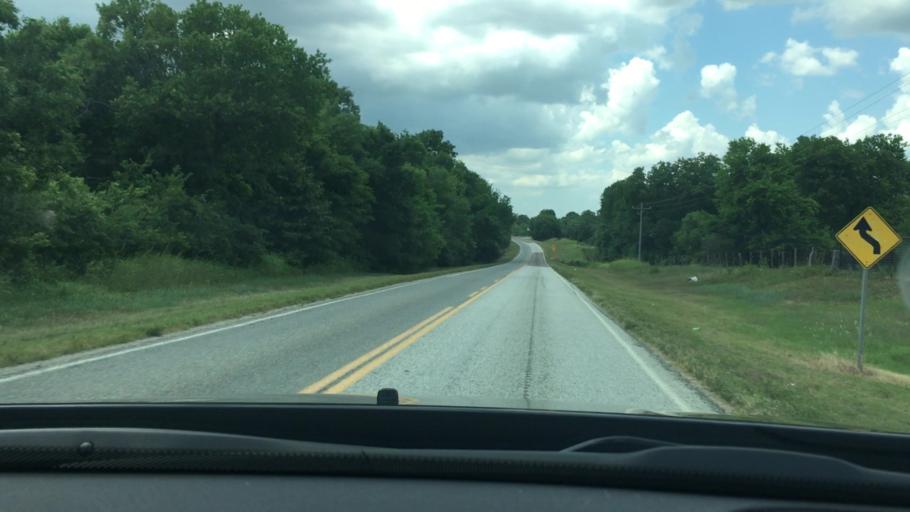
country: US
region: Oklahoma
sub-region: Pontotoc County
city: Ada
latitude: 34.5161
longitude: -96.6306
